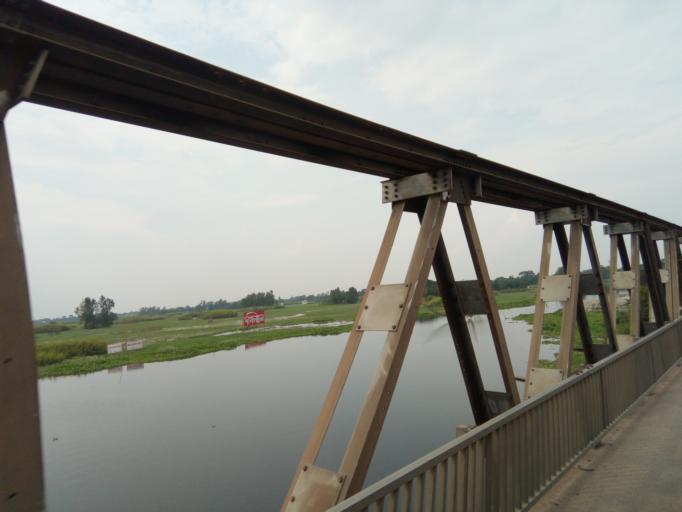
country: BD
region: Dhaka
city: Dohar
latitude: 23.5690
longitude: 90.3011
